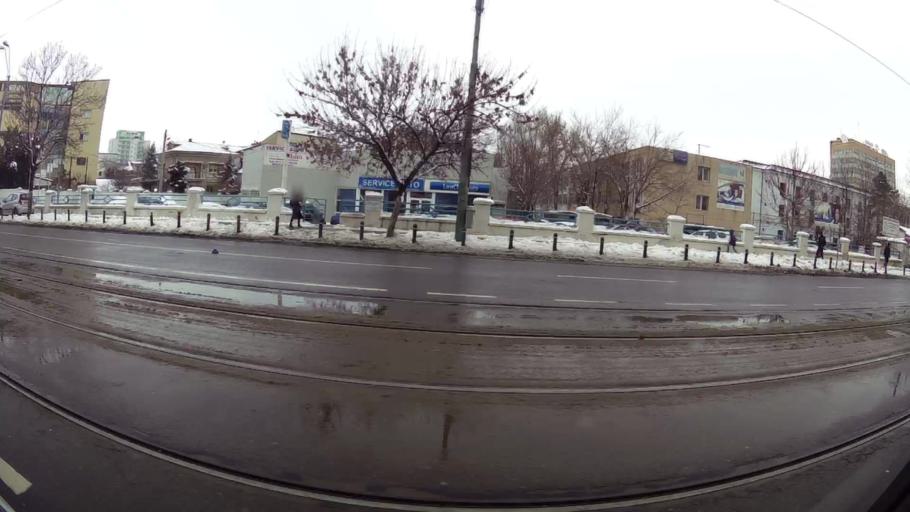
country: RO
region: Bucuresti
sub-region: Municipiul Bucuresti
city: Bucuresti
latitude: 44.3974
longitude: 26.1121
